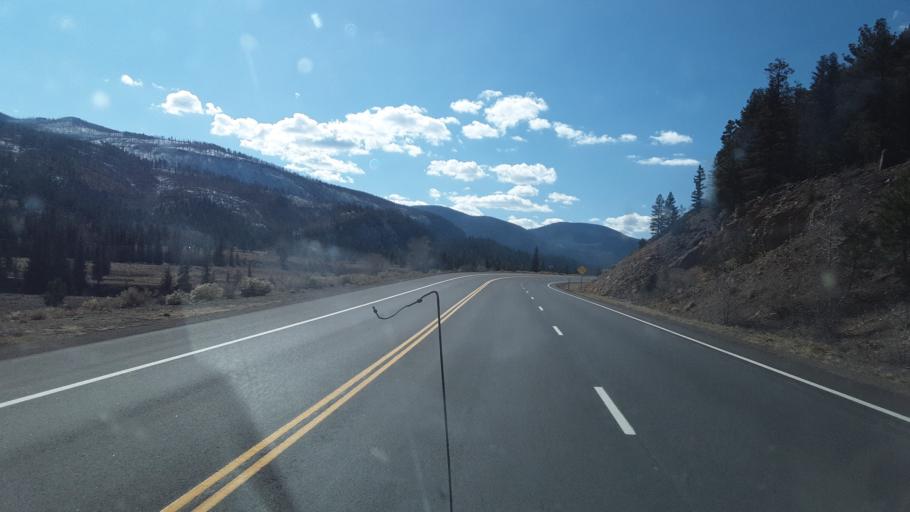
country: US
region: Colorado
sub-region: Rio Grande County
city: Del Norte
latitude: 37.6452
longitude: -106.6619
